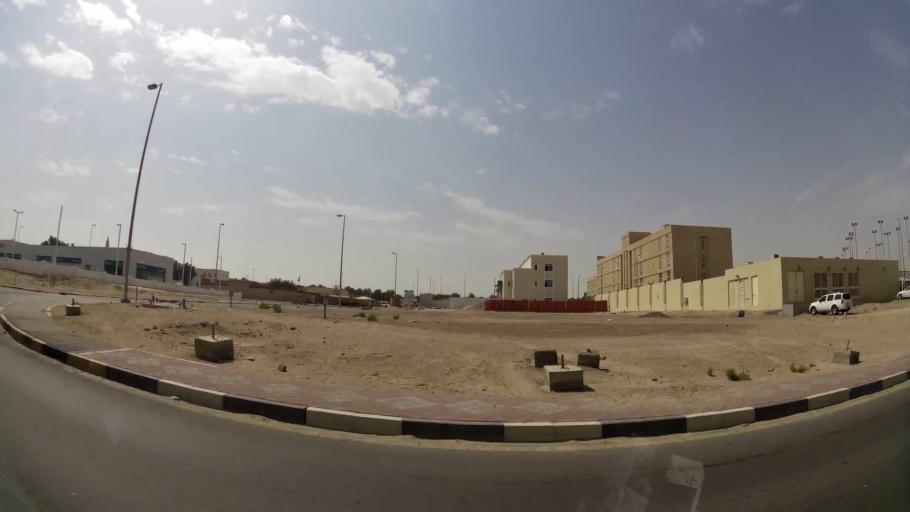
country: AE
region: Abu Dhabi
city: Abu Dhabi
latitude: 24.3049
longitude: 54.6212
